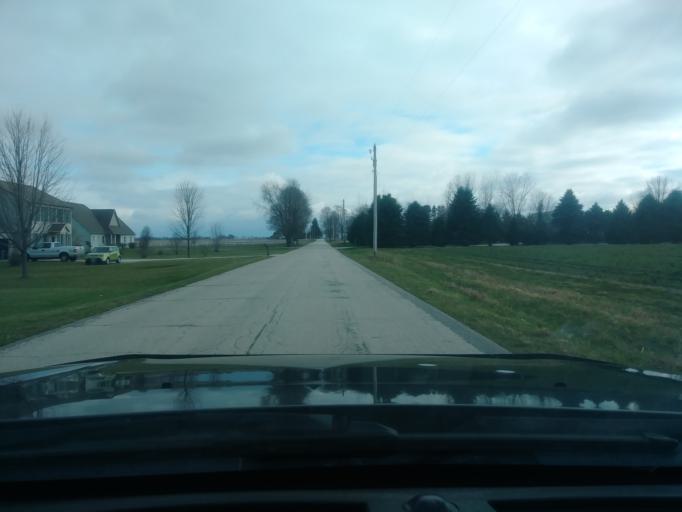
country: US
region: Indiana
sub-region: LaPorte County
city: LaPorte
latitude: 41.5856
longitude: -86.7980
